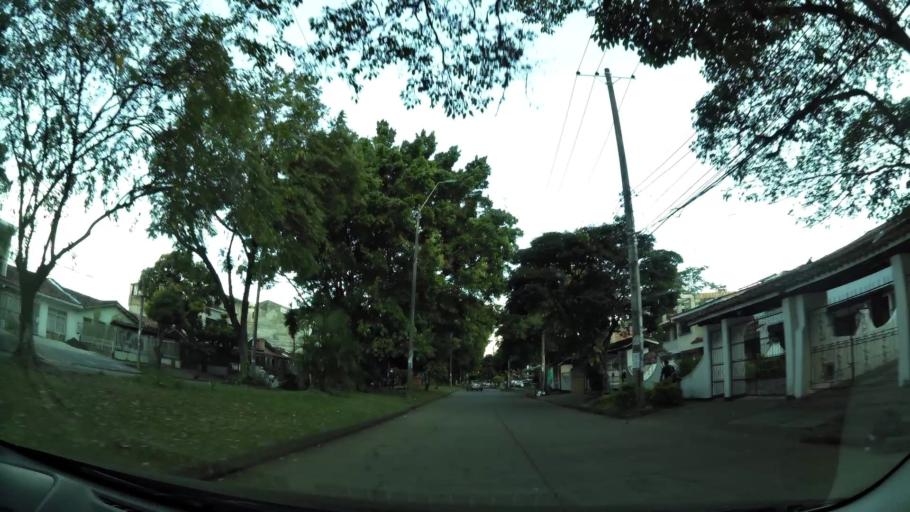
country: CO
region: Valle del Cauca
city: Cali
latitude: 3.4046
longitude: -76.5512
